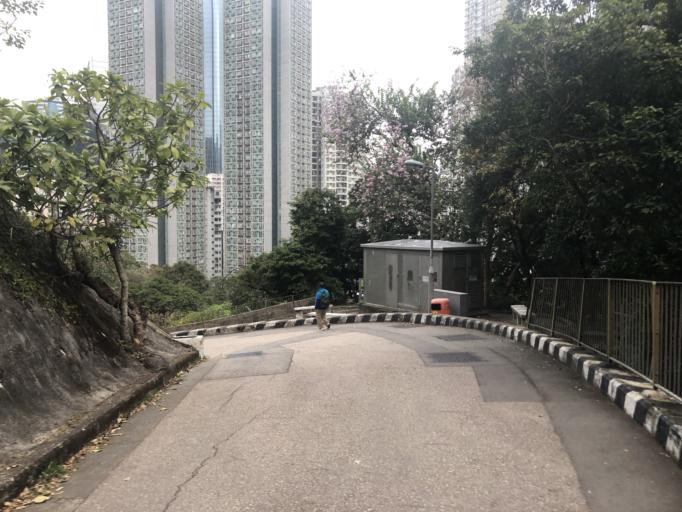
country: HK
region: Wanchai
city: Wan Chai
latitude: 22.2816
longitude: 114.2121
